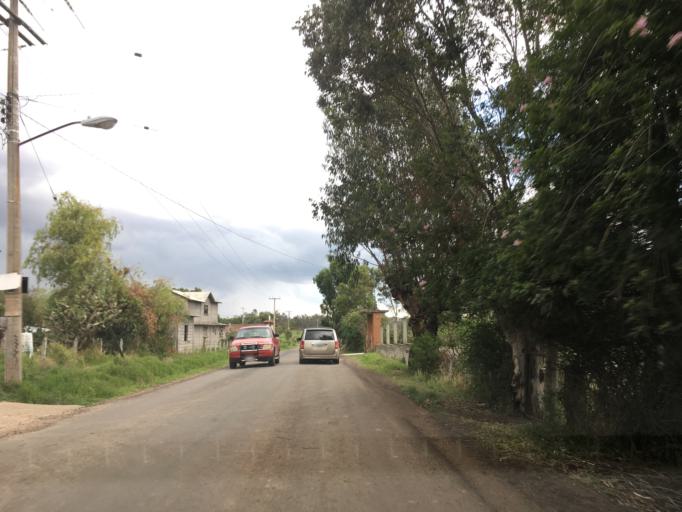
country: MX
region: Michoacan
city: Acuitzio del Canje
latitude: 19.5628
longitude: -101.2754
